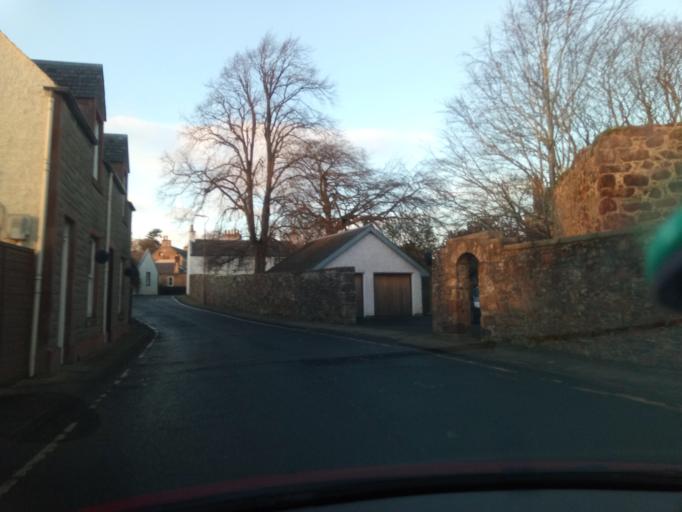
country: GB
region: Scotland
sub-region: The Scottish Borders
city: Melrose
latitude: 55.6002
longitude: -2.7443
